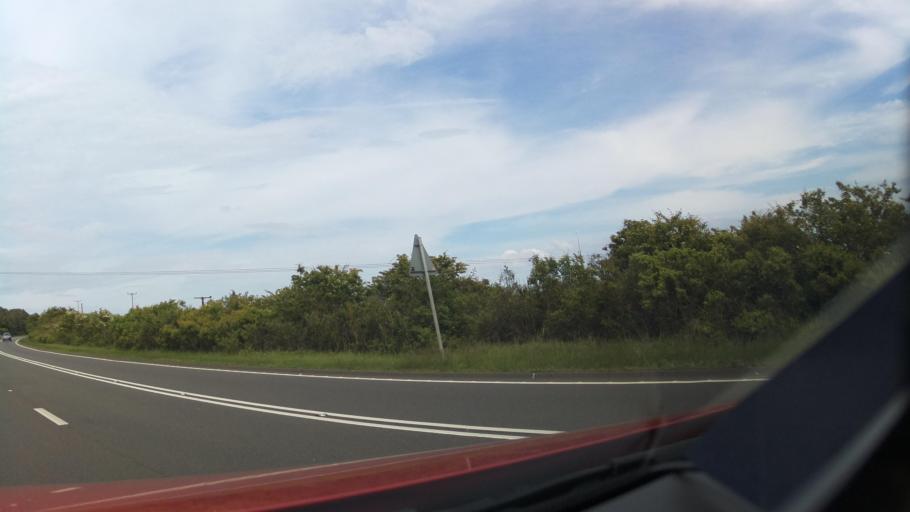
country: GB
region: England
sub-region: Northumberland
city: Berwick-Upon-Tweed
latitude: 55.7730
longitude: -2.0417
